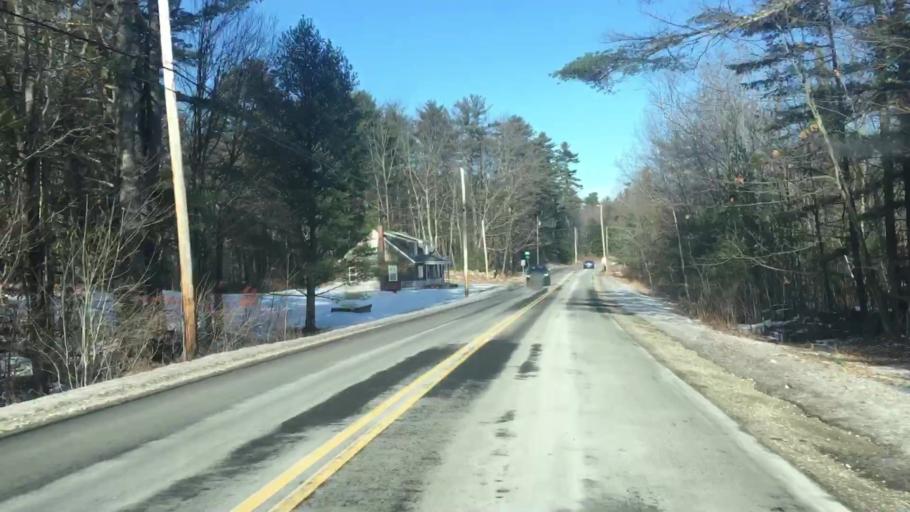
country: US
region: Maine
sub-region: Androscoggin County
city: Auburn
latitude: 44.1140
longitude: -70.2700
